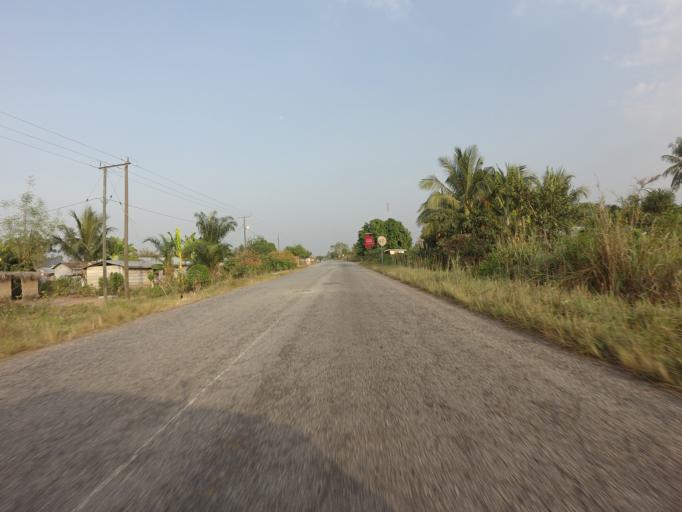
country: GH
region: Volta
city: Ho
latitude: 6.5756
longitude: 0.3303
